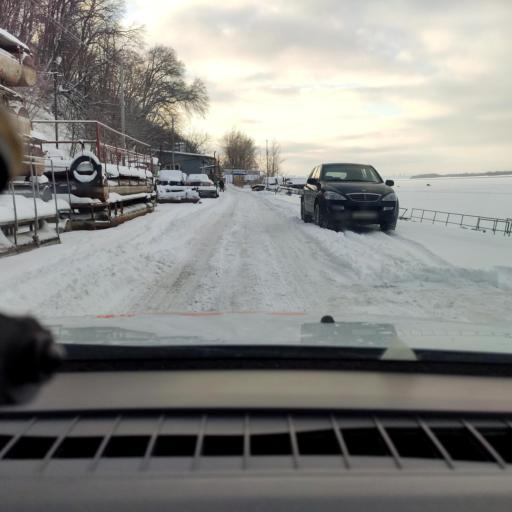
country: RU
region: Samara
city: Samara
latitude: 53.2878
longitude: 50.1912
